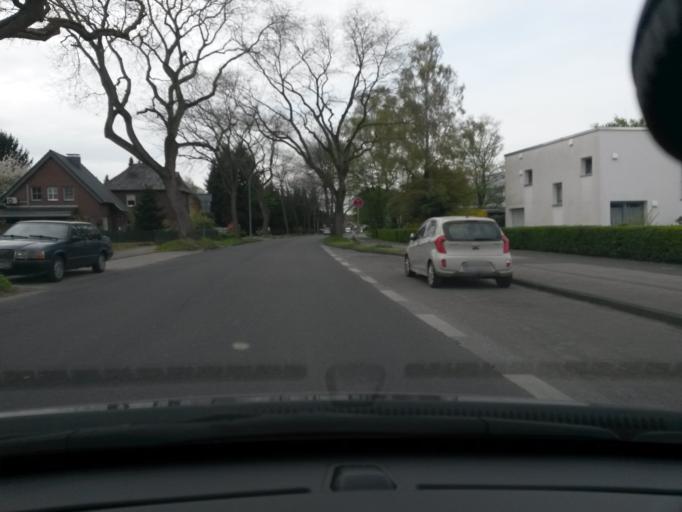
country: DE
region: North Rhine-Westphalia
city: Wegberg
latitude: 51.1358
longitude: 6.2795
